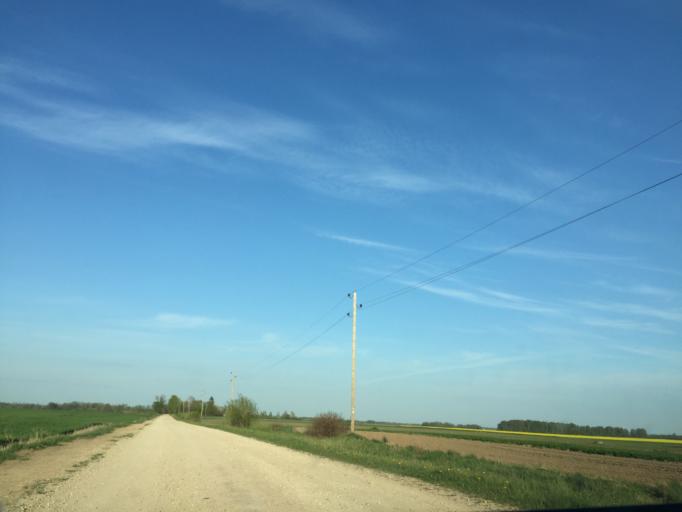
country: LV
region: Bauskas Rajons
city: Bauska
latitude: 56.2964
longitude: 24.2633
